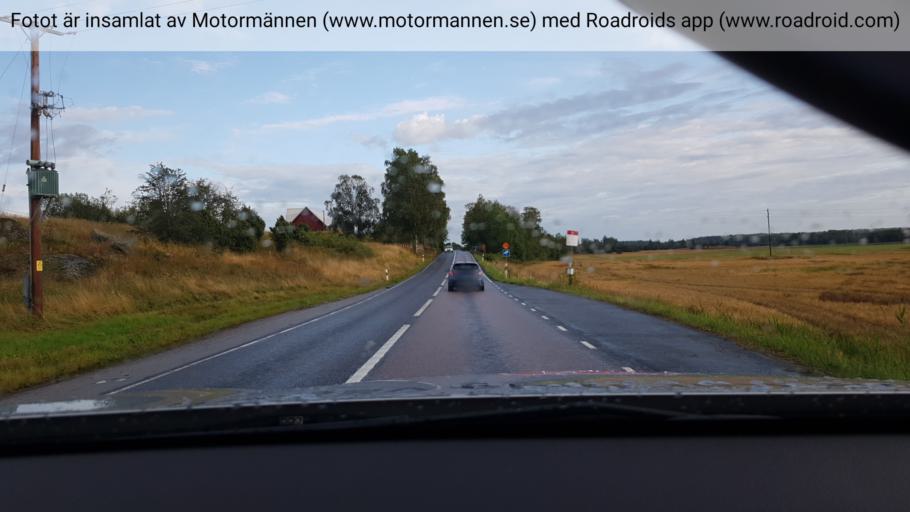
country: SE
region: Stockholm
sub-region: Norrtalje Kommun
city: Norrtalje
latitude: 59.7993
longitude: 18.6569
